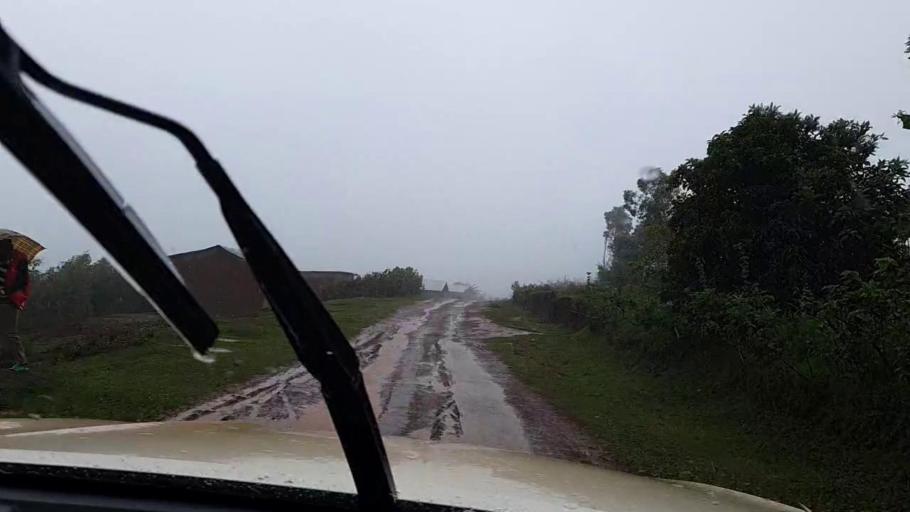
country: RW
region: Northern Province
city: Byumba
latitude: -1.7352
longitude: 30.0122
